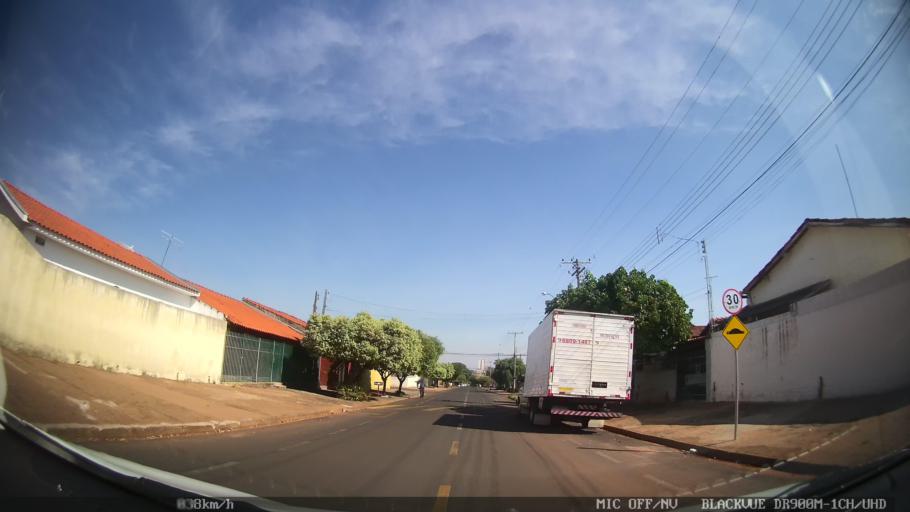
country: BR
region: Sao Paulo
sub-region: Sao Jose Do Rio Preto
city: Sao Jose do Rio Preto
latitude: -20.7870
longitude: -49.4019
